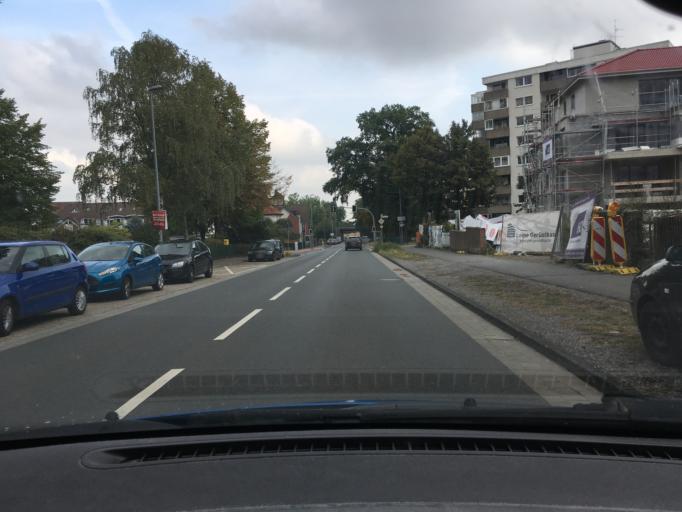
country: DE
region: Lower Saxony
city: Barsinghausen
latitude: 52.3063
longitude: 9.4600
